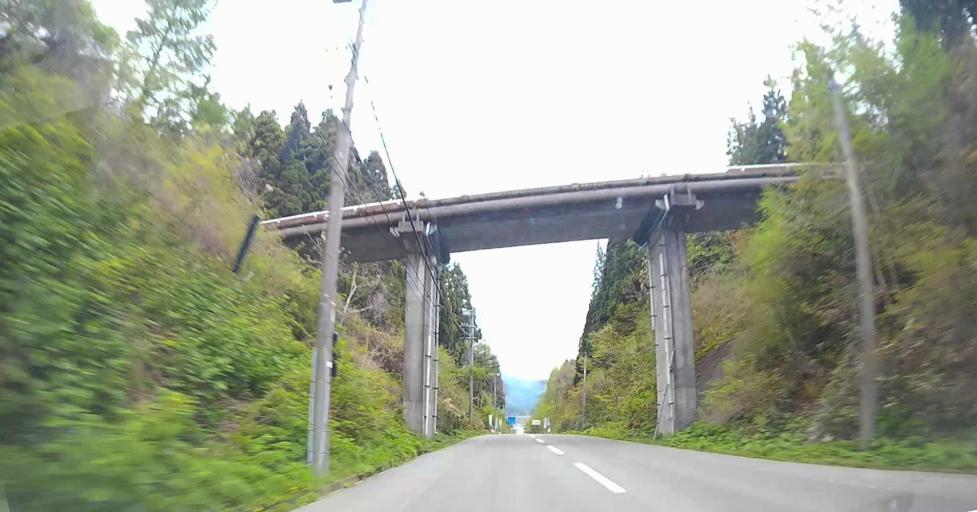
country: JP
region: Aomori
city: Goshogawara
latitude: 41.1771
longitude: 140.4855
